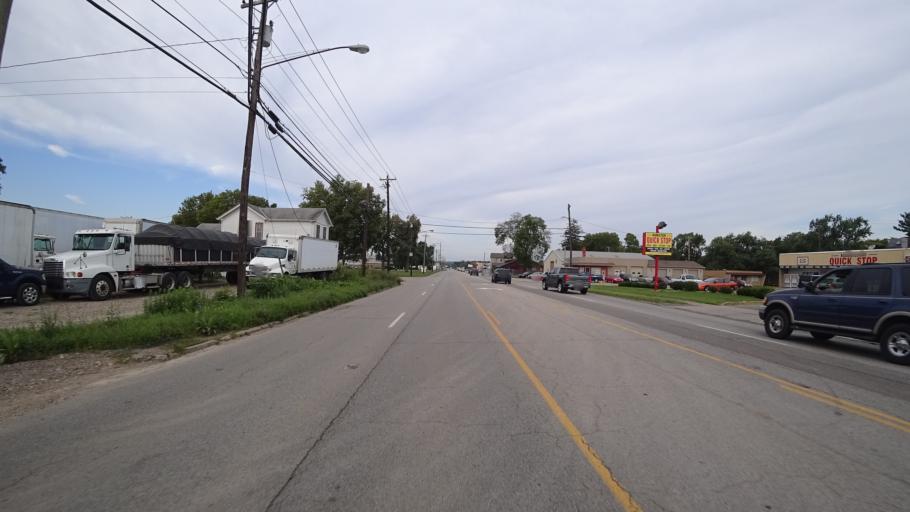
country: US
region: Ohio
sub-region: Butler County
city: Hamilton
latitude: 39.4036
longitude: -84.5316
